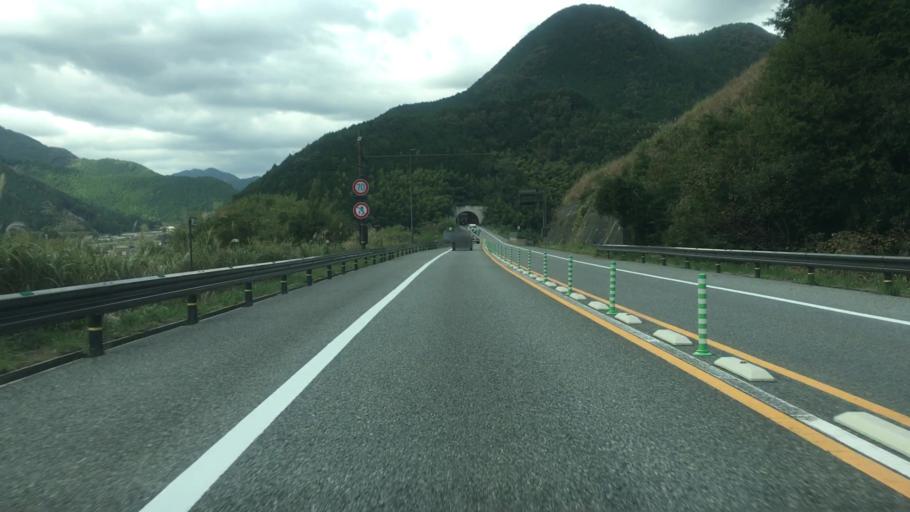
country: JP
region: Kyoto
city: Fukuchiyama
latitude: 35.2693
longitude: 134.9976
